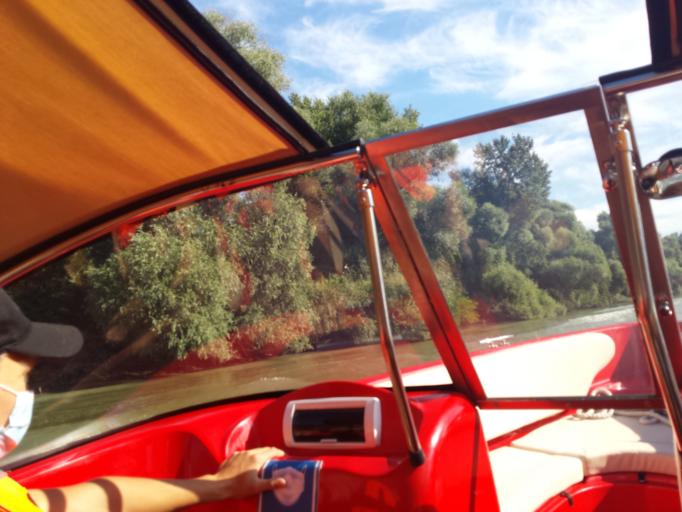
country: RO
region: Tulcea
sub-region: Comuna Nufaru
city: Malcoci
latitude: 45.2132
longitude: 28.8648
